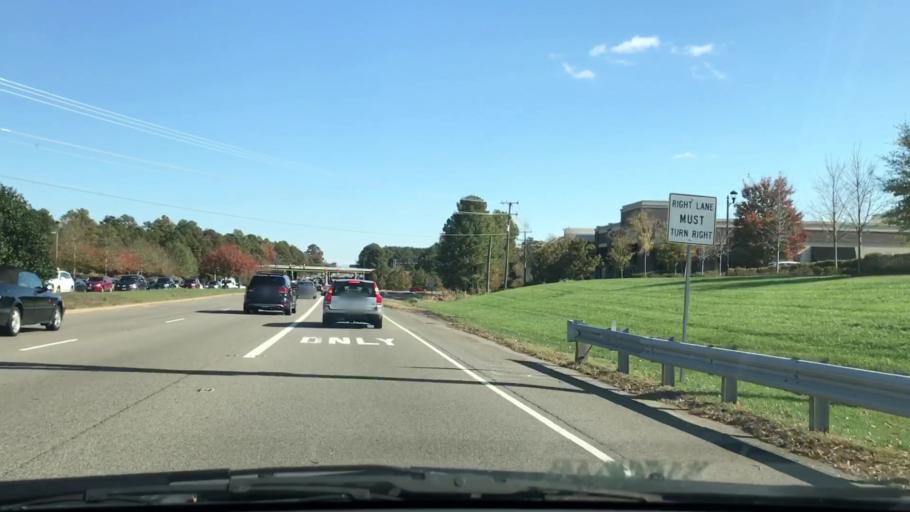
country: US
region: Virginia
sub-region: Henrico County
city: Short Pump
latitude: 37.6488
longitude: -77.5988
